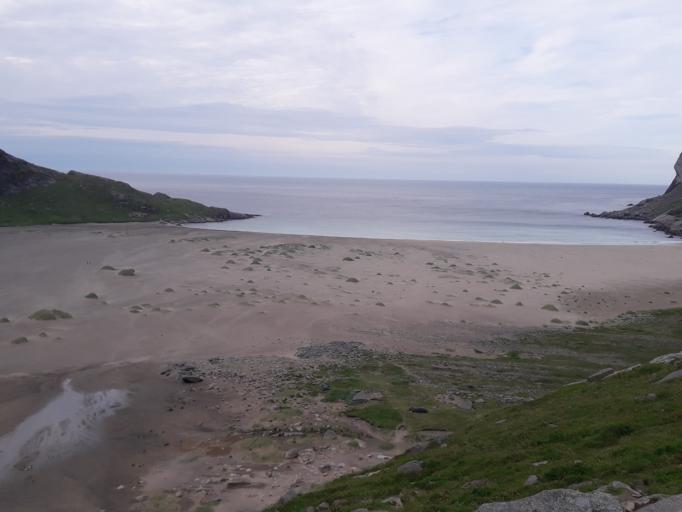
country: NO
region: Nordland
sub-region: Moskenes
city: Reine
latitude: 67.9740
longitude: 12.9751
